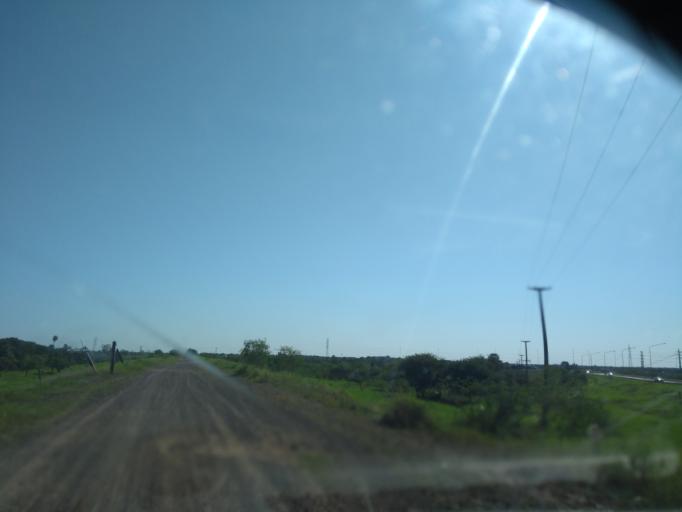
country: AR
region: Chaco
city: Barranqueras
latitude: -27.4458
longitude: -58.8943
